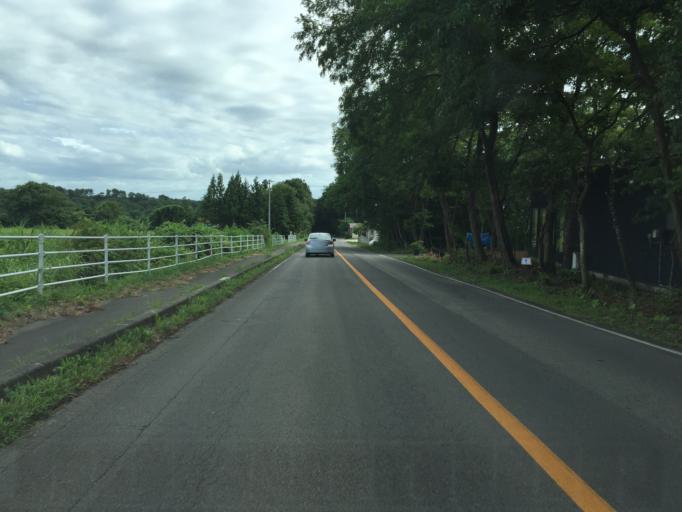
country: JP
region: Fukushima
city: Nihommatsu
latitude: 37.5968
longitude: 140.3565
